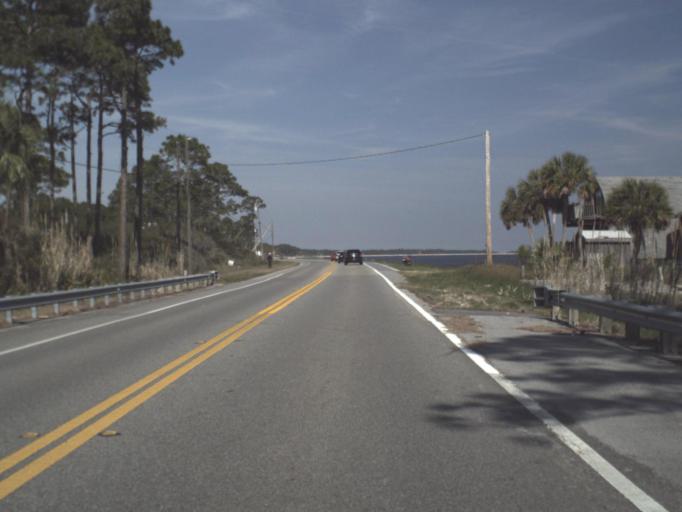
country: US
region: Florida
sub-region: Franklin County
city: Carrabelle
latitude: 29.8154
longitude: -84.7156
